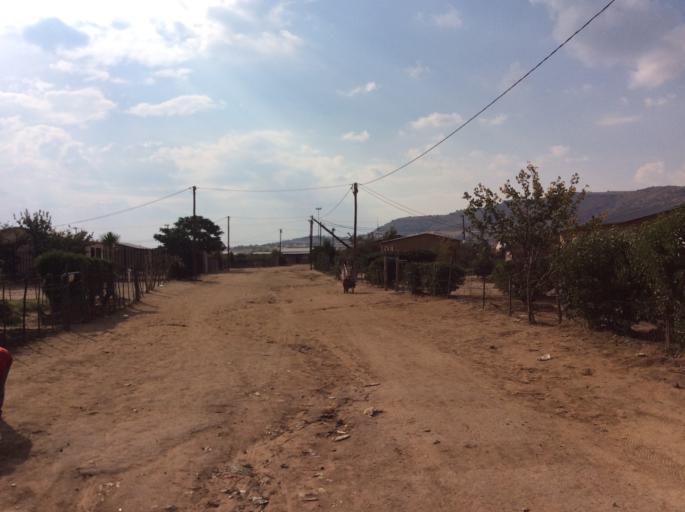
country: LS
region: Mafeteng
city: Mafeteng
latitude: -29.7116
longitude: 27.0118
